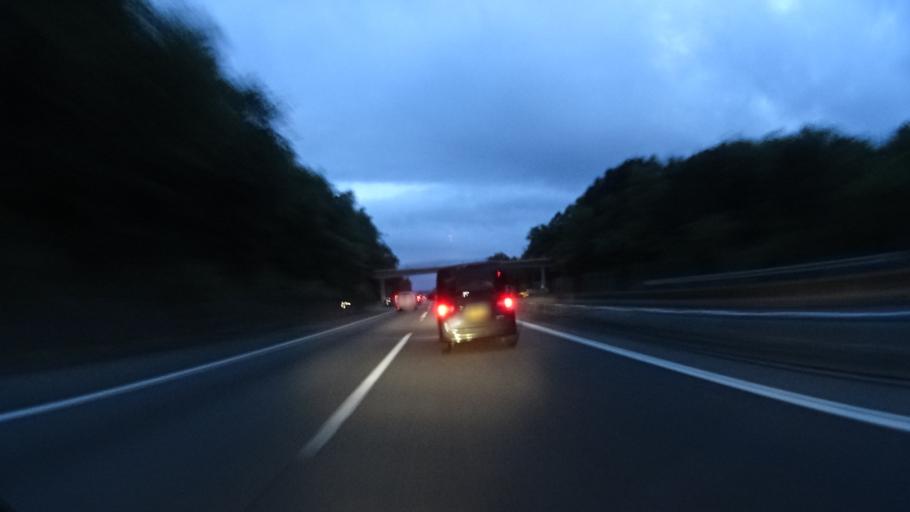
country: JP
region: Shiga Prefecture
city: Youkaichi
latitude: 35.1495
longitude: 136.2798
